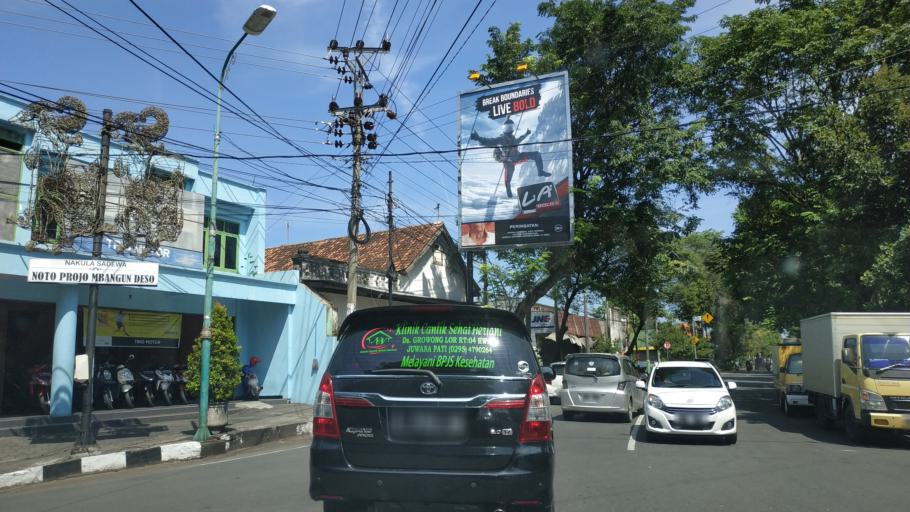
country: ID
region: Central Java
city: Baran
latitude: -6.7545
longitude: 111.0471
